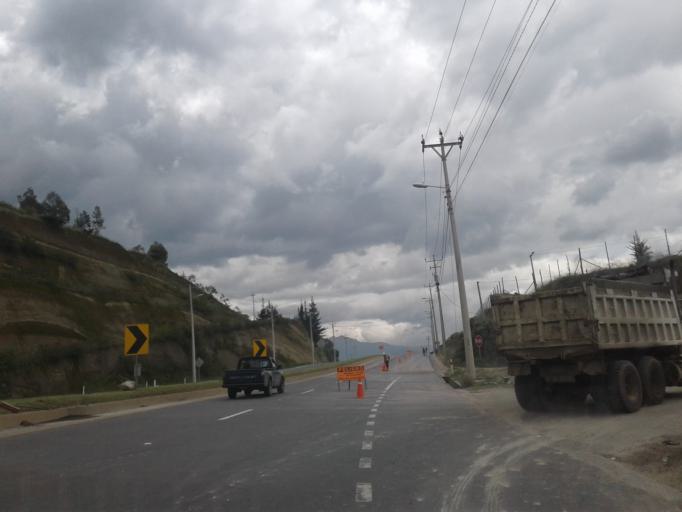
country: EC
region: Pichincha
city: Sangolqui
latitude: -0.2980
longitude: -78.3573
